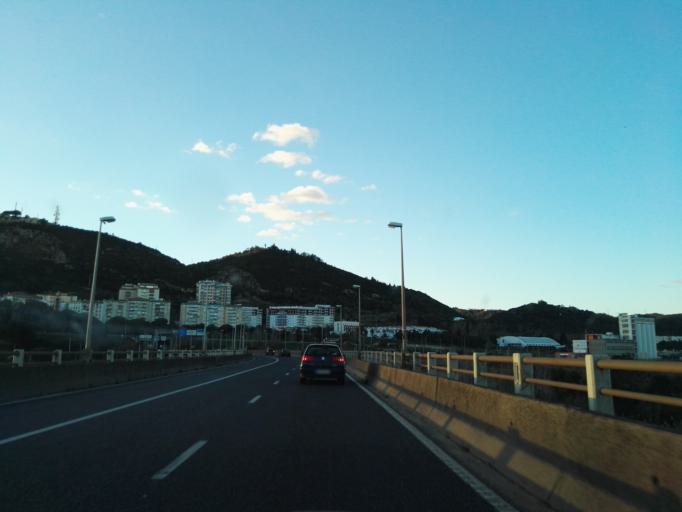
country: PT
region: Lisbon
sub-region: Vila Franca de Xira
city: Vila Franca de Xira
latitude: 38.9594
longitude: -8.9827
